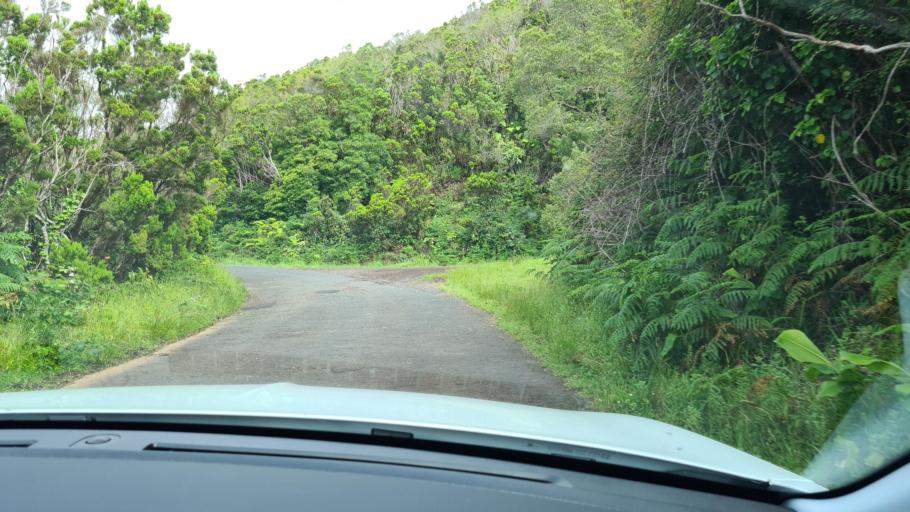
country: PT
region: Azores
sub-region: Sao Roque do Pico
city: Sao Roque do Pico
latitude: 38.6603
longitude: -28.1210
